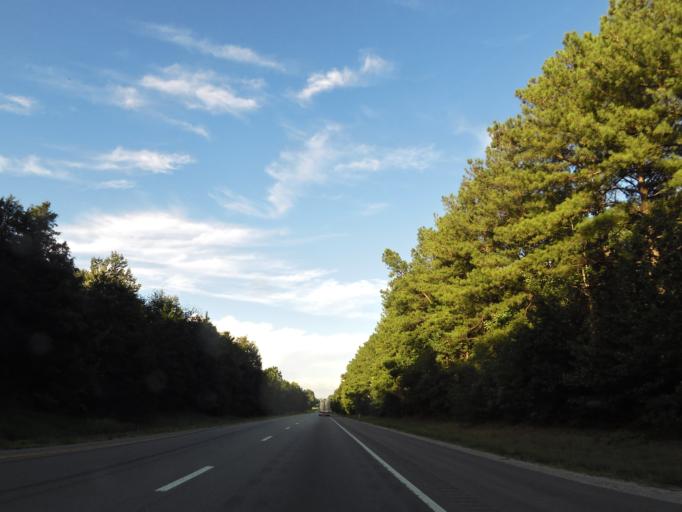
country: US
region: Tennessee
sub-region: Putnam County
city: Baxter
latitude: 36.1277
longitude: -85.6718
